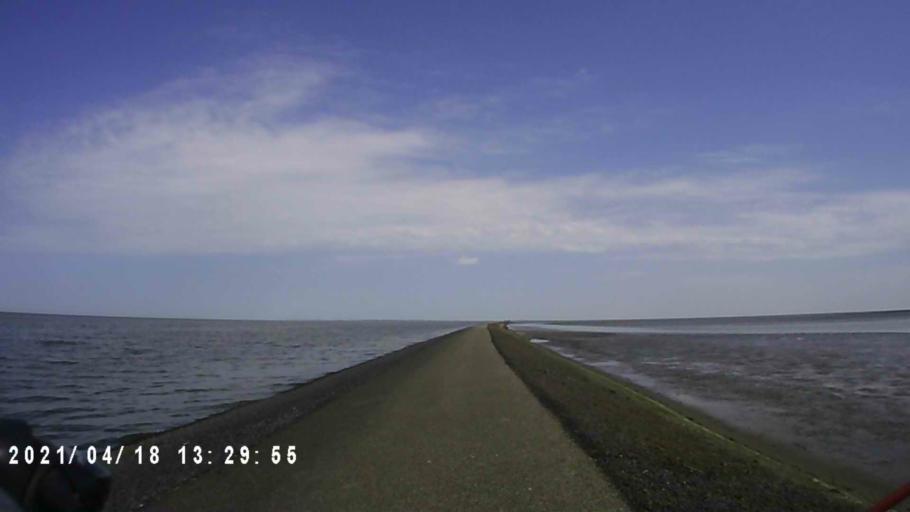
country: NL
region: Friesland
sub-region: Gemeente Dongeradeel
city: Anjum
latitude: 53.4107
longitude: 6.0940
